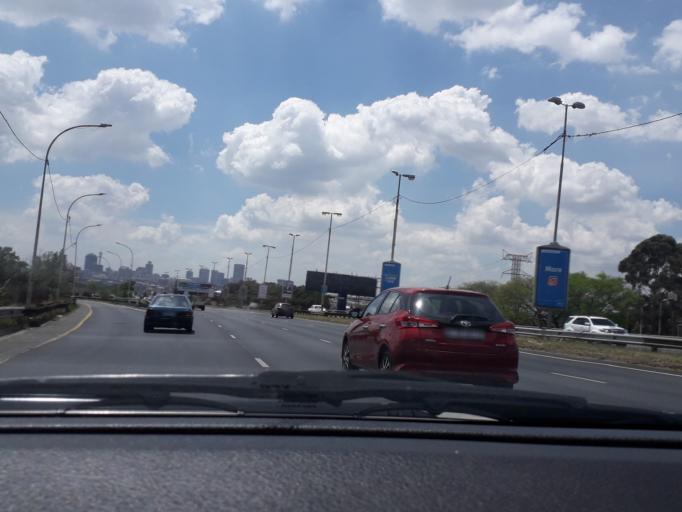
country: ZA
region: Gauteng
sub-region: City of Johannesburg Metropolitan Municipality
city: Johannesburg
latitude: -26.2380
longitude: 28.0162
